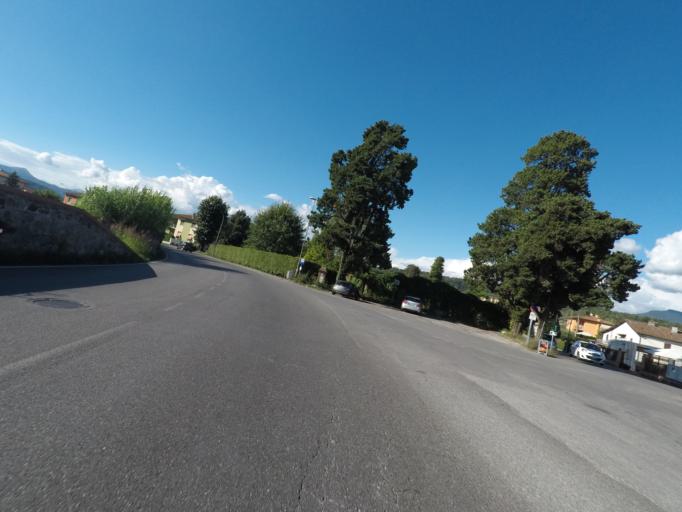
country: IT
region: Tuscany
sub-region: Provincia di Lucca
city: Lucca
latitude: 43.8698
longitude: 10.5071
